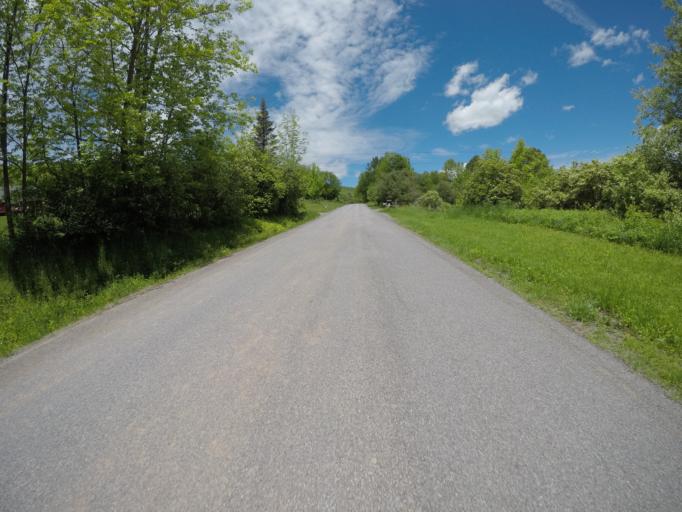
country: US
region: New York
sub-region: Delaware County
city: Stamford
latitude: 42.2704
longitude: -74.5192
